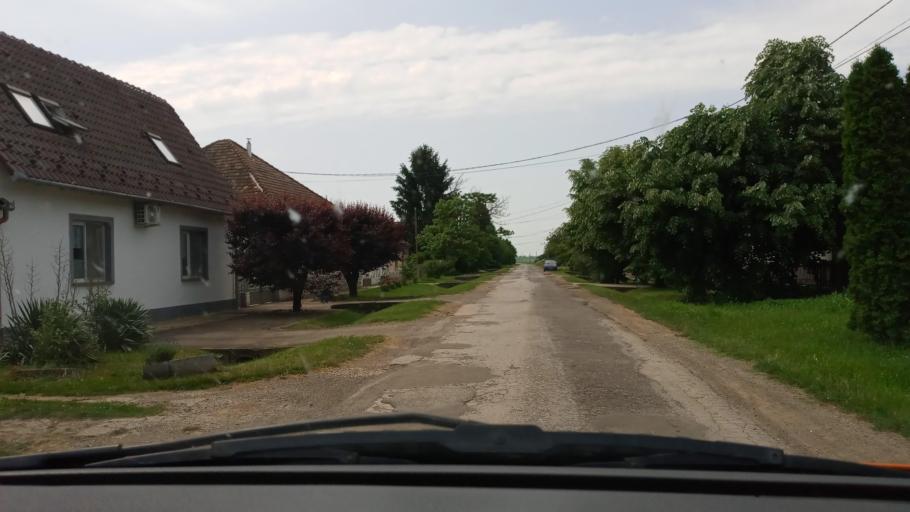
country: HU
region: Baranya
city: Szentlorinc
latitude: 46.0022
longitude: 18.0491
